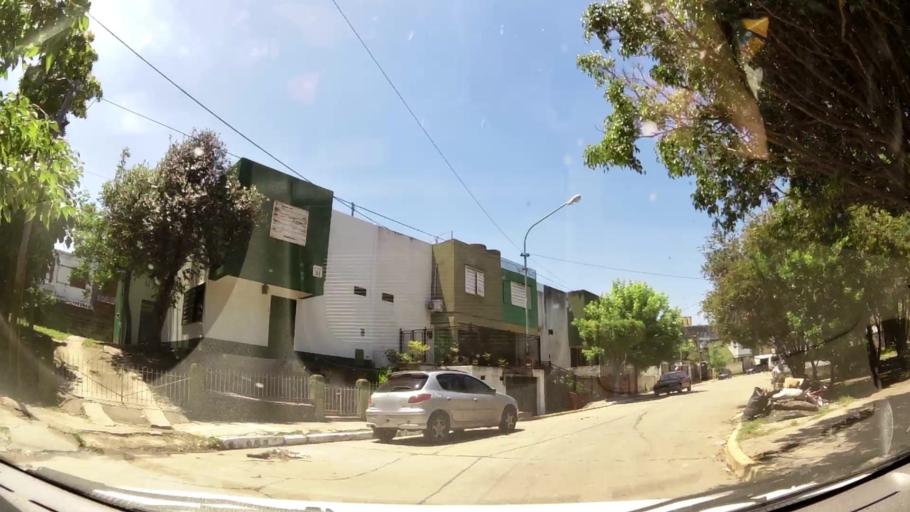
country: AR
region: Buenos Aires
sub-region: Partido de Merlo
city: Merlo
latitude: -34.6517
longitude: -58.7097
